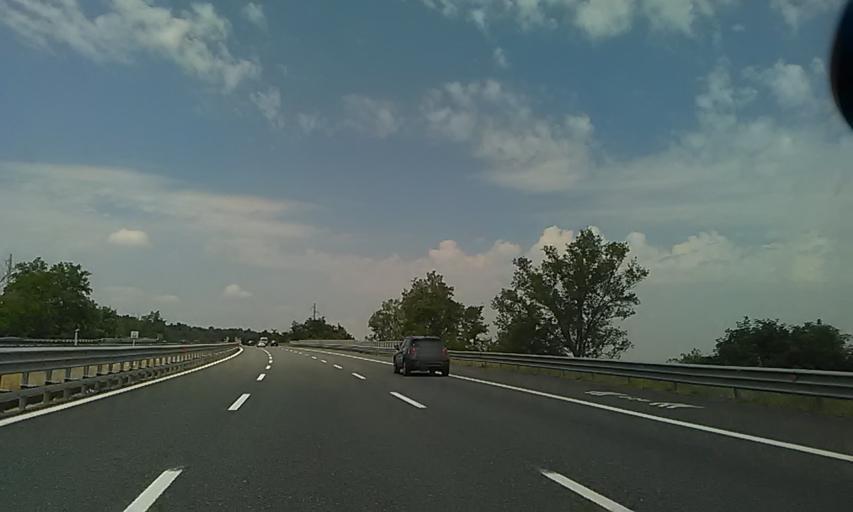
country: IT
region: Piedmont
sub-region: Provincia di Alessandria
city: Predosa
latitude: 44.7360
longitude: 8.6589
